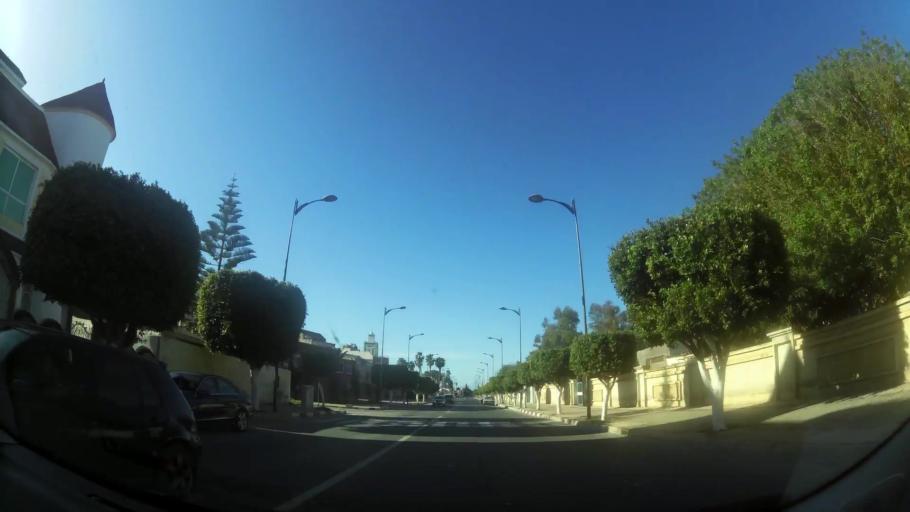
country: MA
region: Oriental
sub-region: Berkane-Taourirt
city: Madagh
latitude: 35.0775
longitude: -2.2162
